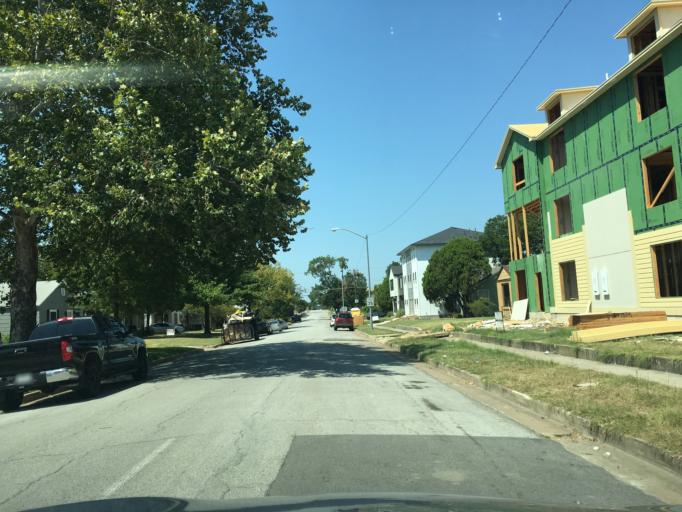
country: US
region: Texas
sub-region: Tarrant County
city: Fort Worth
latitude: 32.7030
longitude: -97.3524
